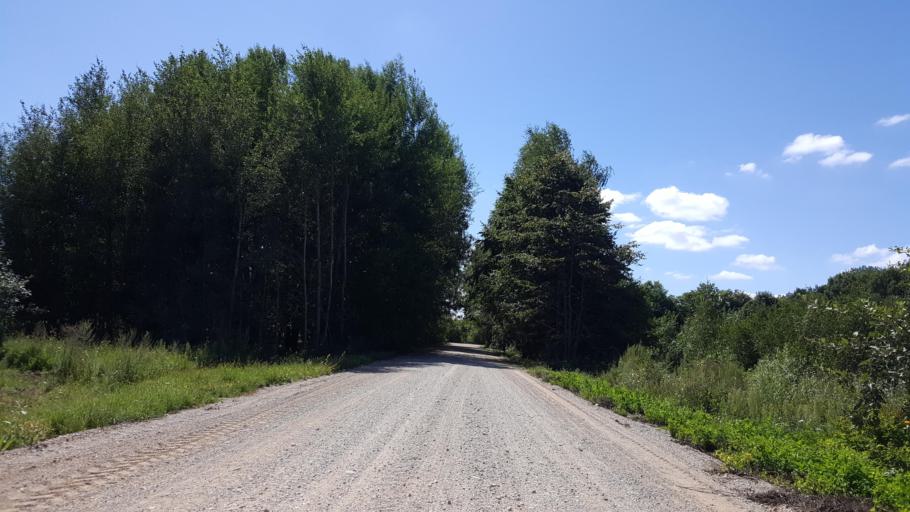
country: BY
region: Brest
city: Horad Kobryn
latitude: 52.3046
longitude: 24.3664
